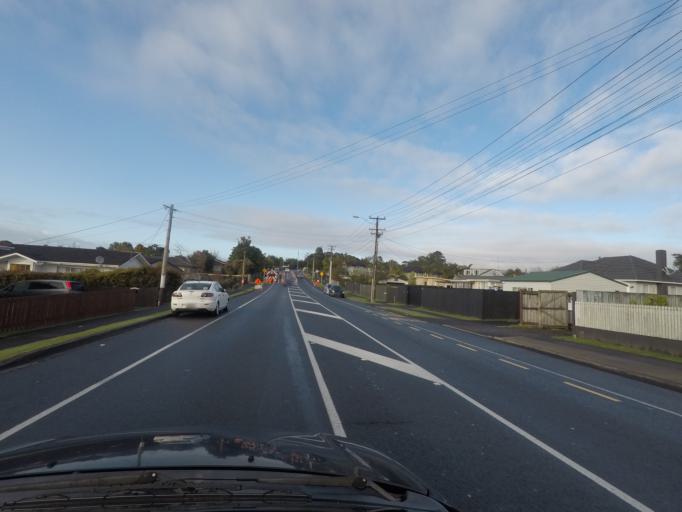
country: NZ
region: Auckland
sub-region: Auckland
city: Waitakere
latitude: -36.8947
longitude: 174.6197
